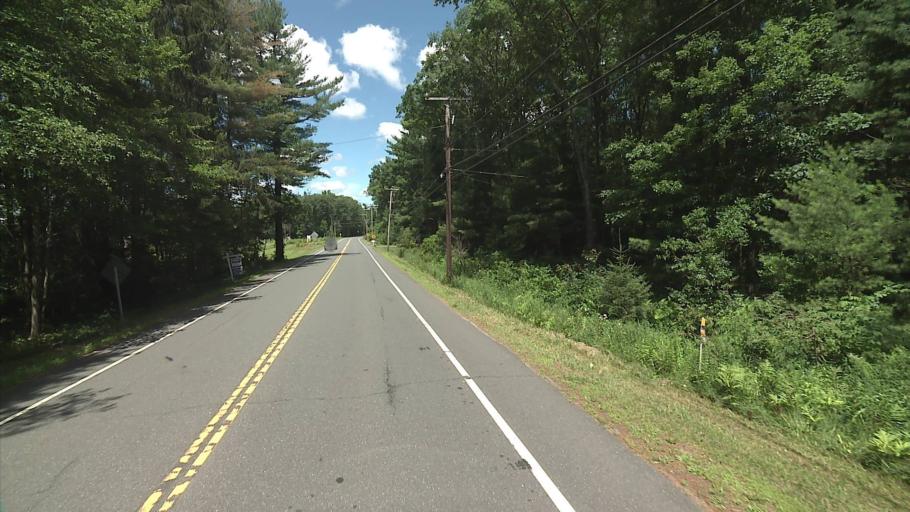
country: US
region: Connecticut
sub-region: Litchfield County
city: New Hartford Center
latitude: 41.8538
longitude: -72.9997
